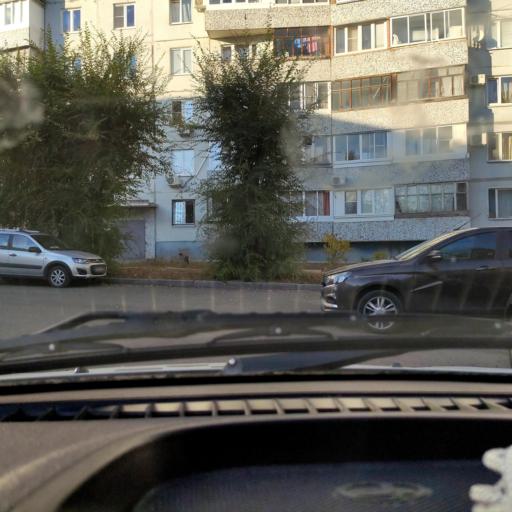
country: RU
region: Samara
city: Zhigulevsk
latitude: 53.4795
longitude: 49.4794
